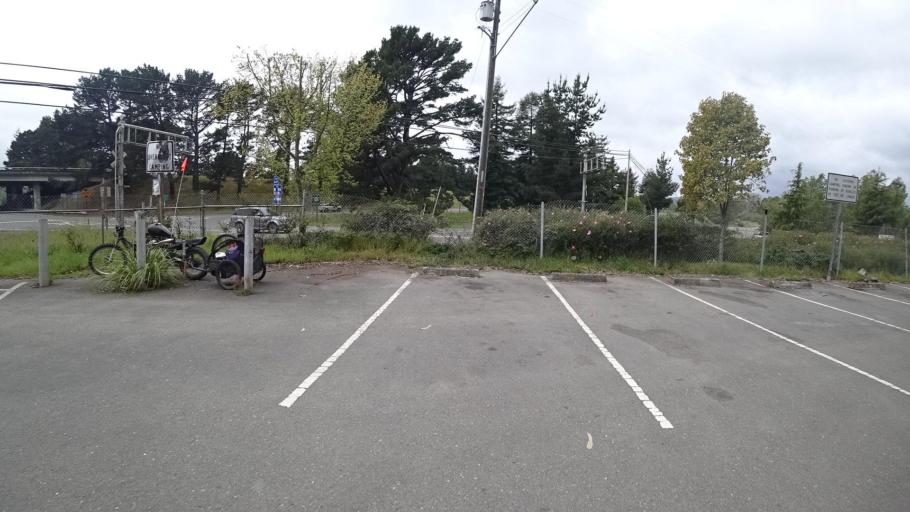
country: US
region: California
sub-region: Humboldt County
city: Fortuna
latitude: 40.5752
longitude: -124.1480
